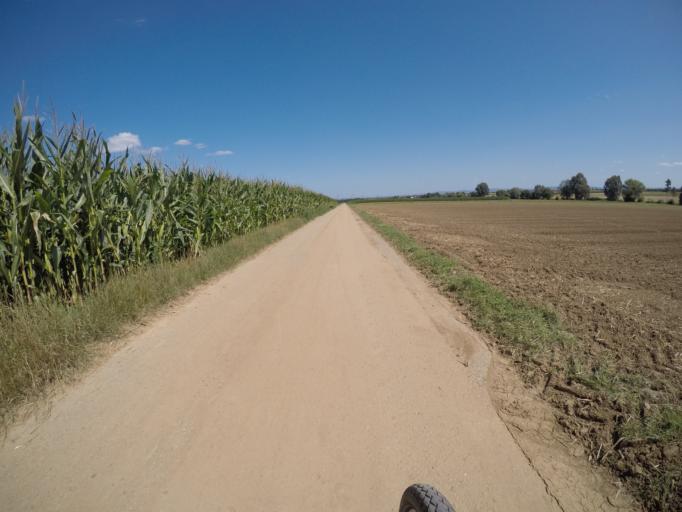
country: DE
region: Baden-Wuerttemberg
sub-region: Regierungsbezirk Stuttgart
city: Ostfildern
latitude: 48.7027
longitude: 9.2402
